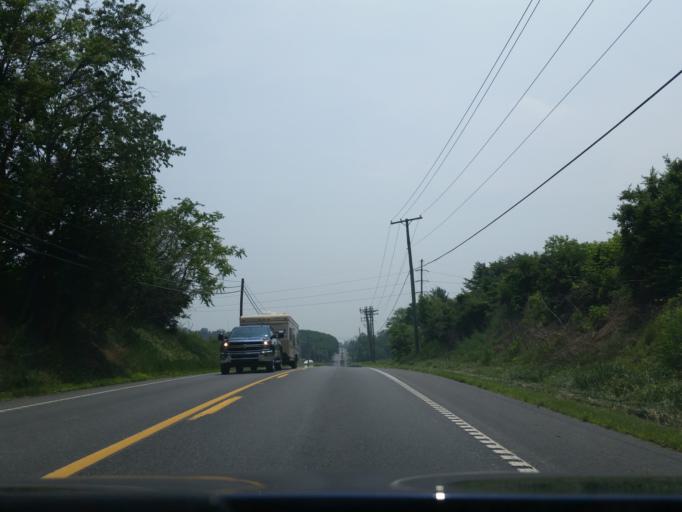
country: US
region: Pennsylvania
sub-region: Lebanon County
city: Jonestown
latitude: 40.4458
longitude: -76.5112
